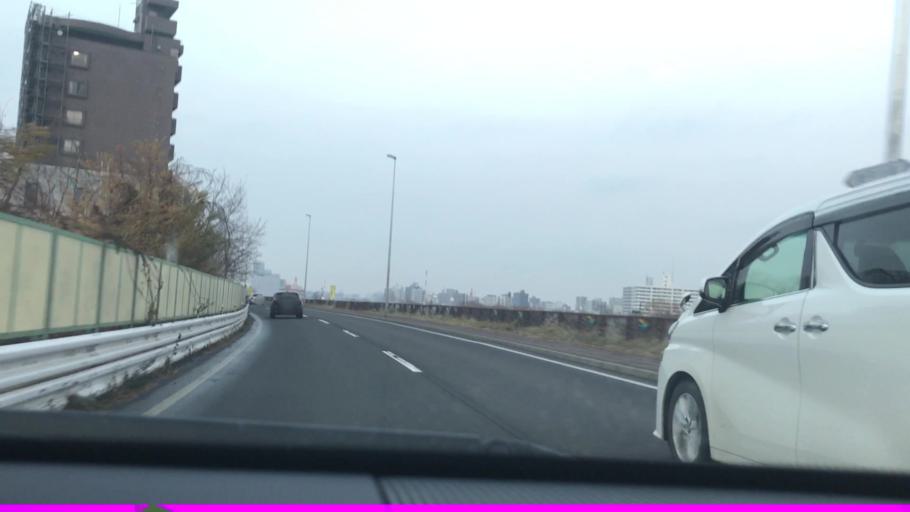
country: JP
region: Hokkaido
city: Sapporo
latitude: 43.0235
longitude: 141.3514
